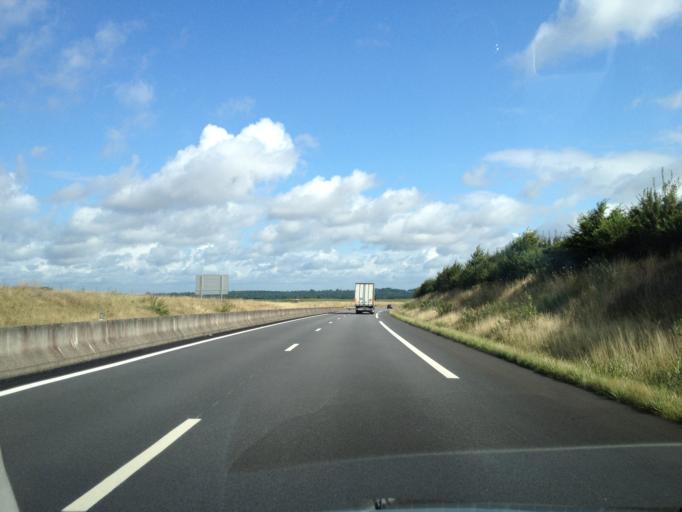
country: FR
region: Haute-Normandie
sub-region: Departement de l'Eure
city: Brionne
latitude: 49.2657
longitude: 0.7656
